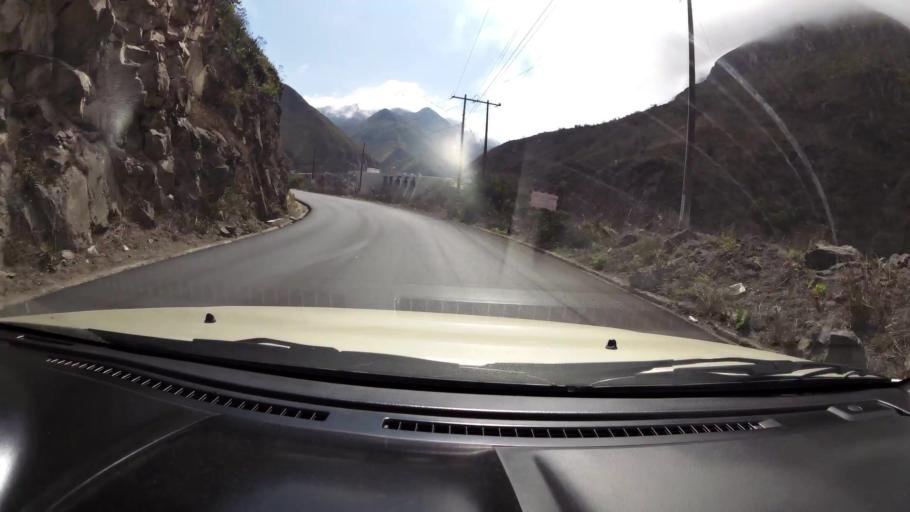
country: EC
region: El Oro
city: Pasaje
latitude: -3.3145
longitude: -79.4881
